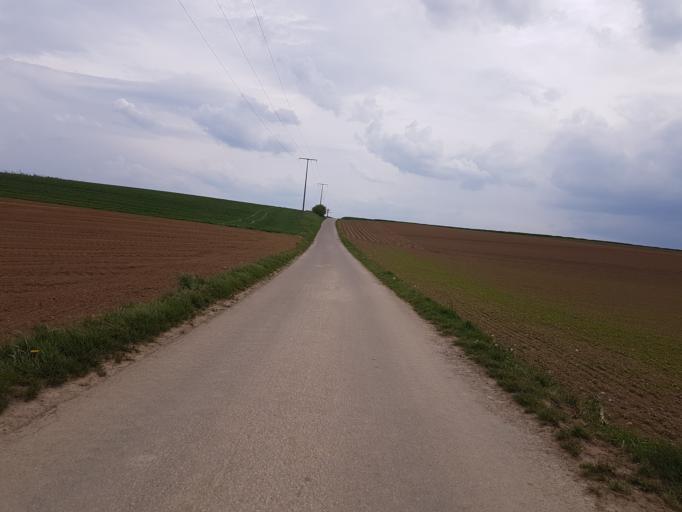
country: DE
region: Baden-Wuerttemberg
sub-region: Regierungsbezirk Stuttgart
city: Bondorf
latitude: 48.5356
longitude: 8.8217
